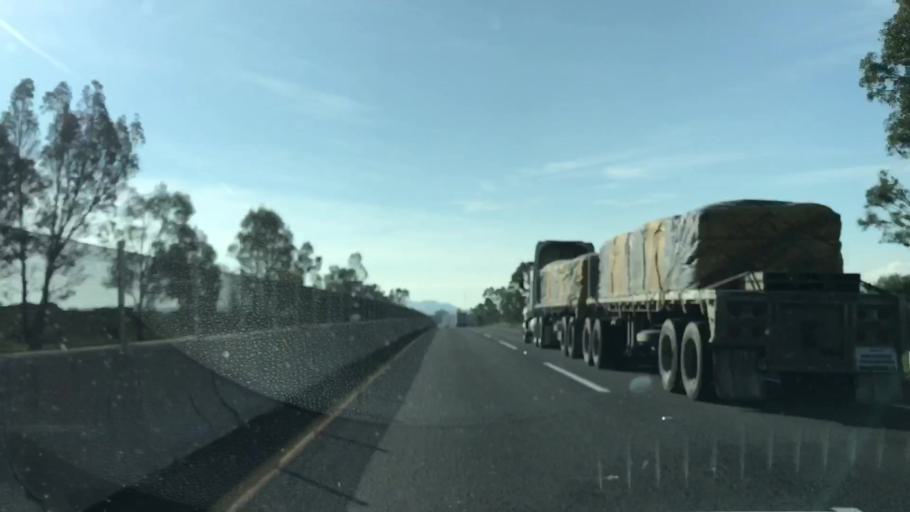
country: MX
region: Jalisco
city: Encarnacion de Diaz
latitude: 21.4667
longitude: -102.2183
